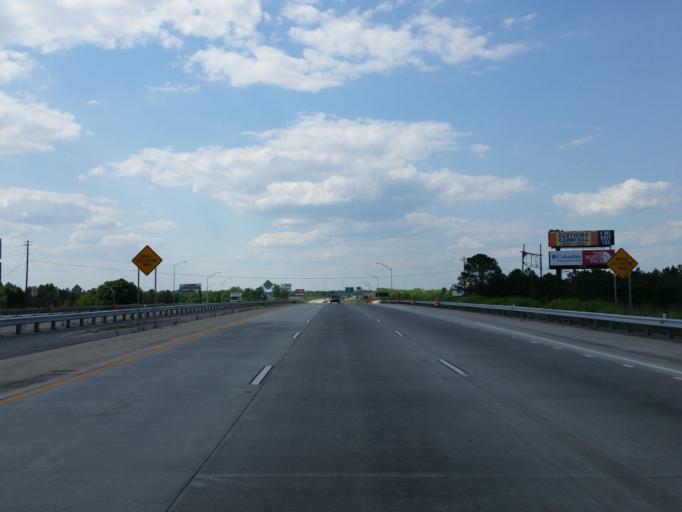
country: US
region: Georgia
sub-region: Dooly County
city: Unadilla
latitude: 32.2456
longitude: -83.7422
